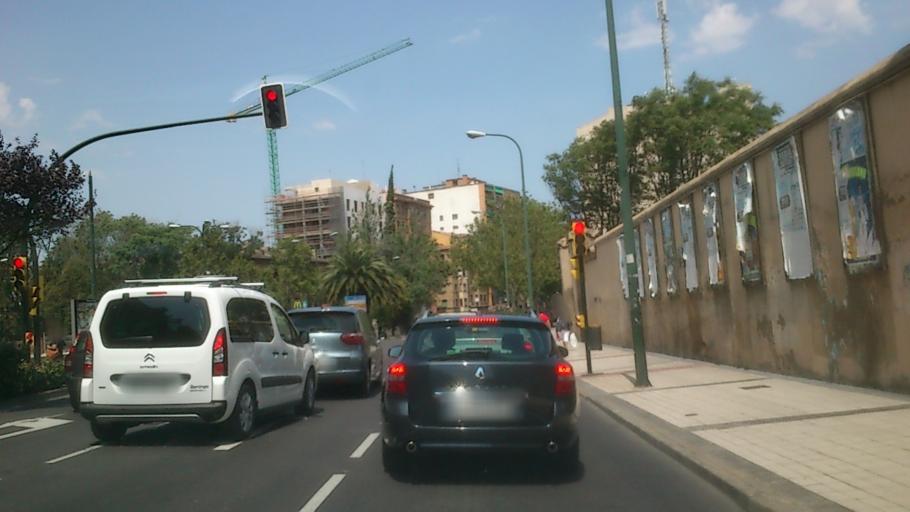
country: ES
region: Aragon
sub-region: Provincia de Zaragoza
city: Almozara
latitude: 41.6534
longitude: -0.8925
